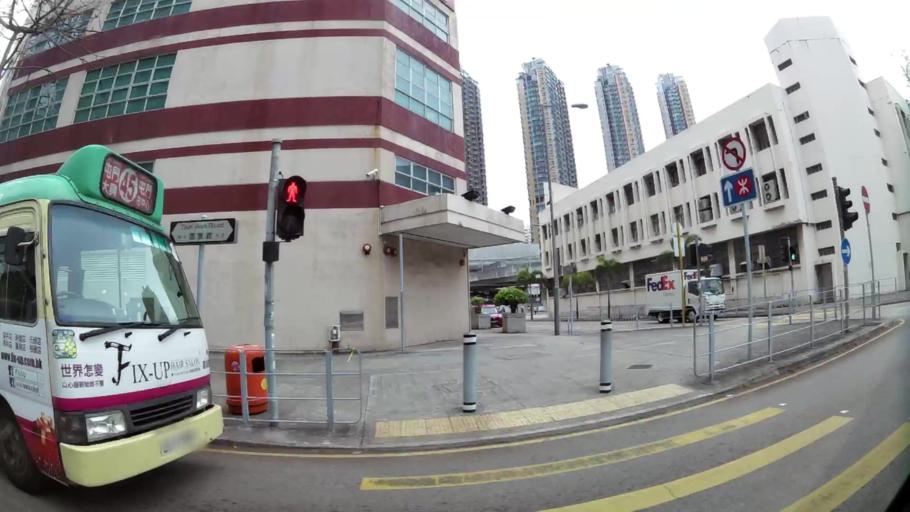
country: HK
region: Tuen Mun
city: Tuen Mun
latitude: 22.3975
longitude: 113.9722
